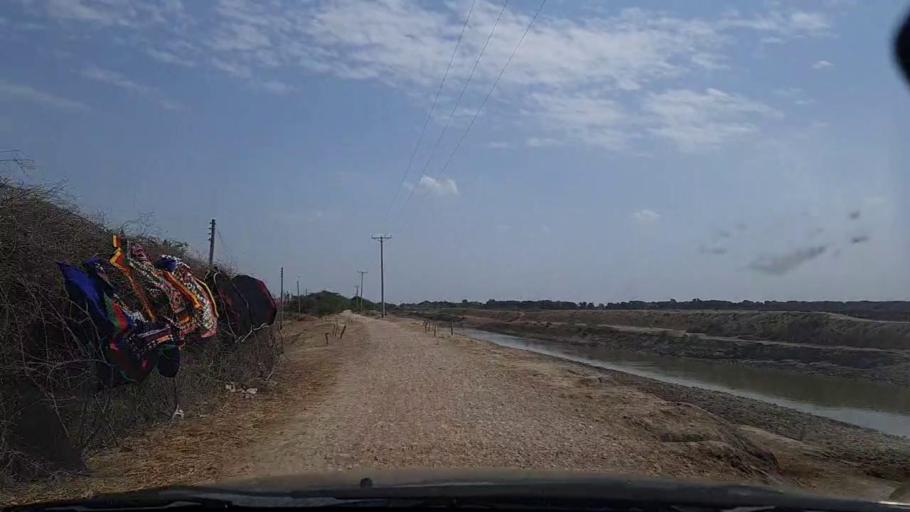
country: PK
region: Sindh
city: Mirpur Batoro
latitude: 24.5679
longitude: 68.1978
